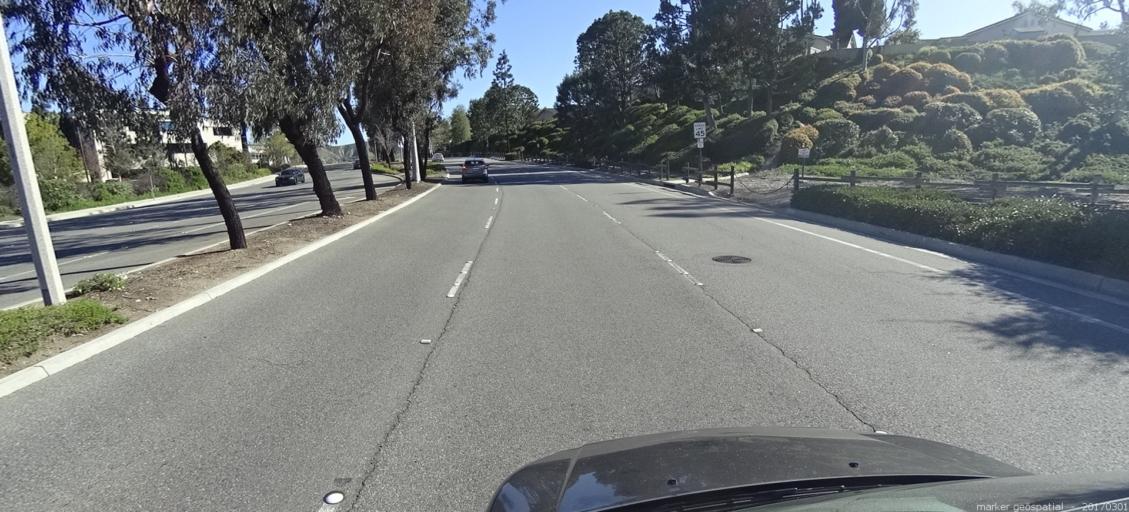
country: US
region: California
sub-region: Orange County
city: Yorba Linda
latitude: 33.8680
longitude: -117.7421
